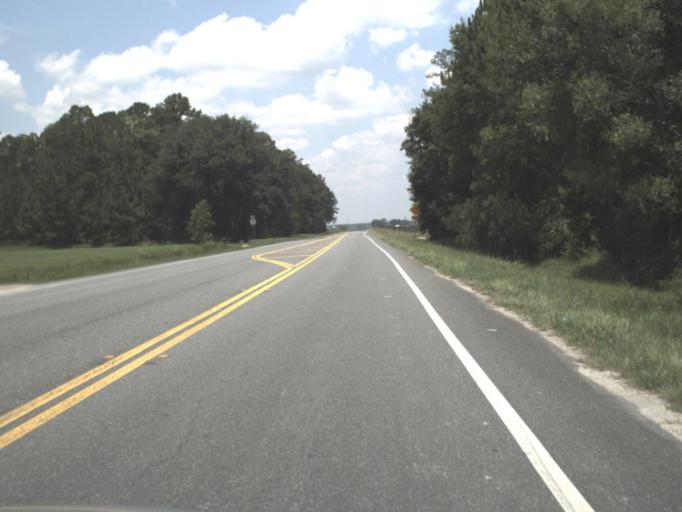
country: US
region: Florida
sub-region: Bradford County
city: Starke
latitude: 30.0402
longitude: -82.1659
